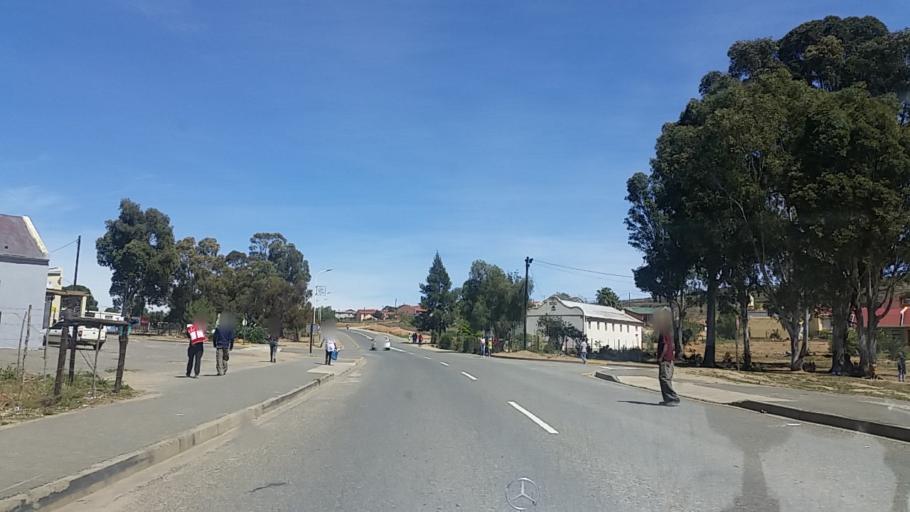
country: ZA
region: Western Cape
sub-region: Eden District Municipality
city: Knysna
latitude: -33.6589
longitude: 23.1180
